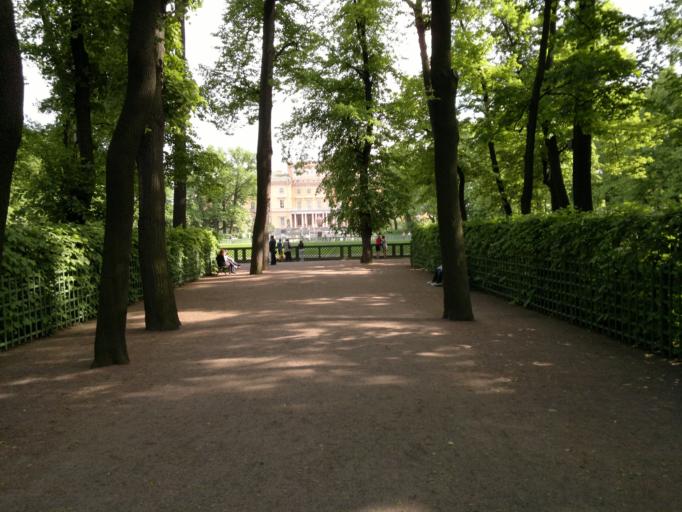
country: RU
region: St.-Petersburg
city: Saint Petersburg
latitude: 59.9428
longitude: 30.3361
